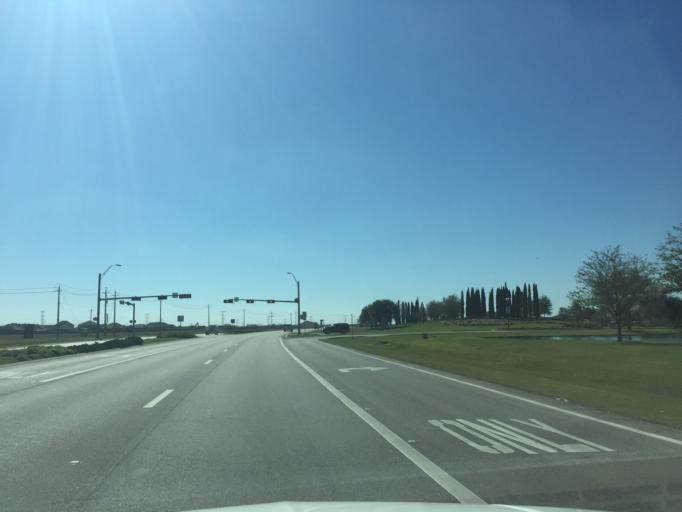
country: US
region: Texas
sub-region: Galveston County
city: Dickinson
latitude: 29.5011
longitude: -95.0469
